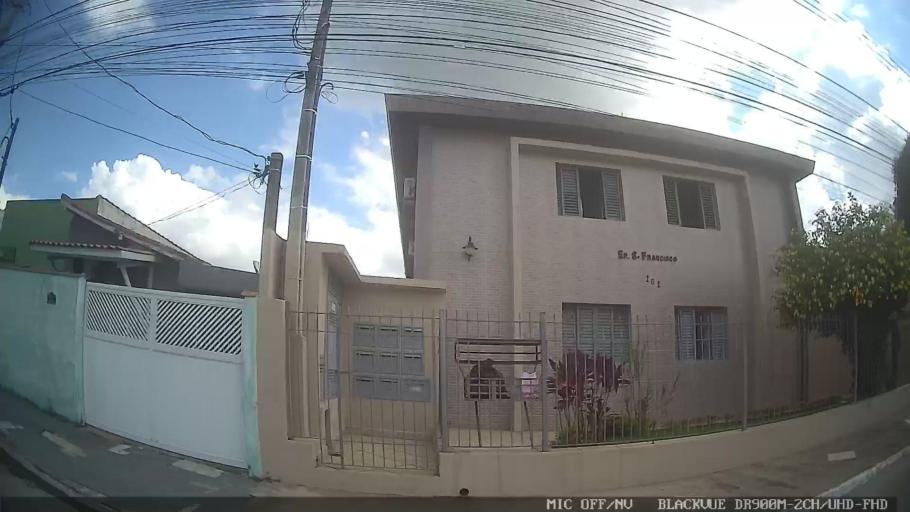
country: BR
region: Sao Paulo
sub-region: Sao Sebastiao
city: Sao Sebastiao
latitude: -23.8002
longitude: -45.4003
